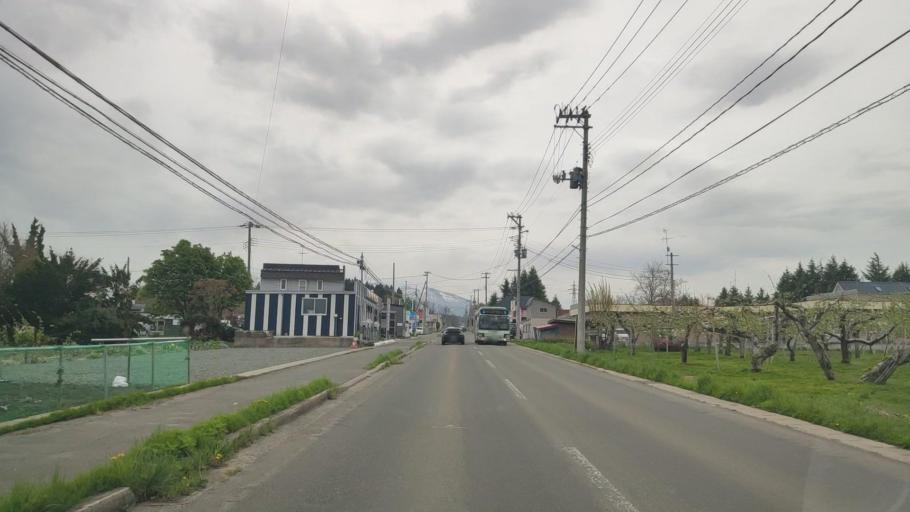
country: JP
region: Aomori
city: Aomori Shi
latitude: 40.7838
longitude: 140.7907
